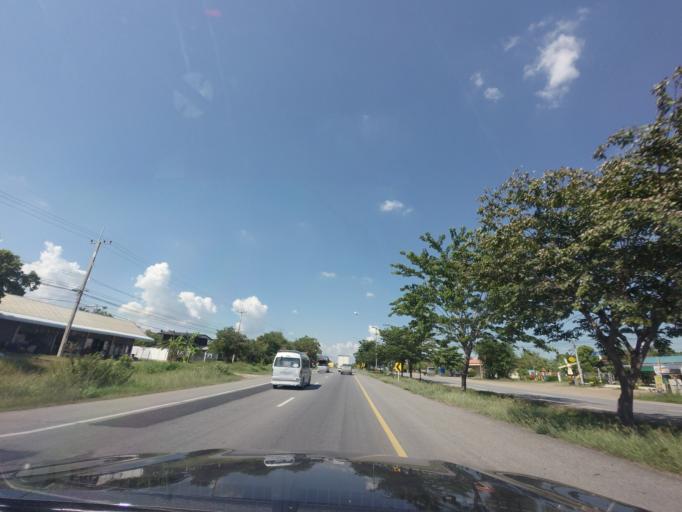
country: TH
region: Nakhon Ratchasima
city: Non Sung
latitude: 15.1664
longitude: 102.3331
